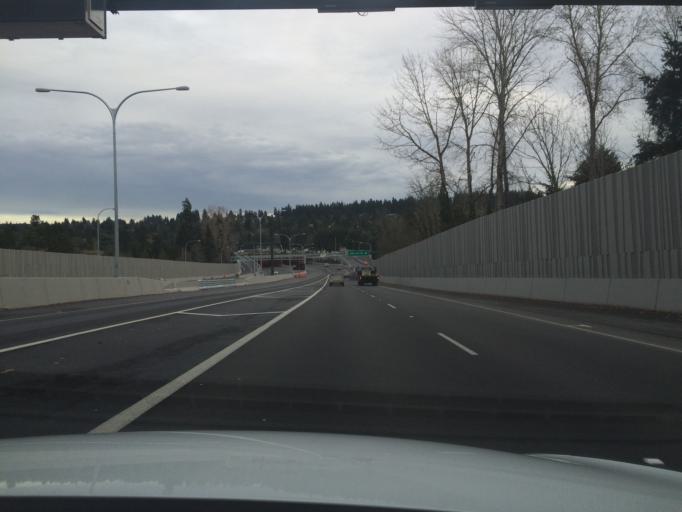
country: US
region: Washington
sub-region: King County
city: Medina
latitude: 47.6364
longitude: -122.2342
